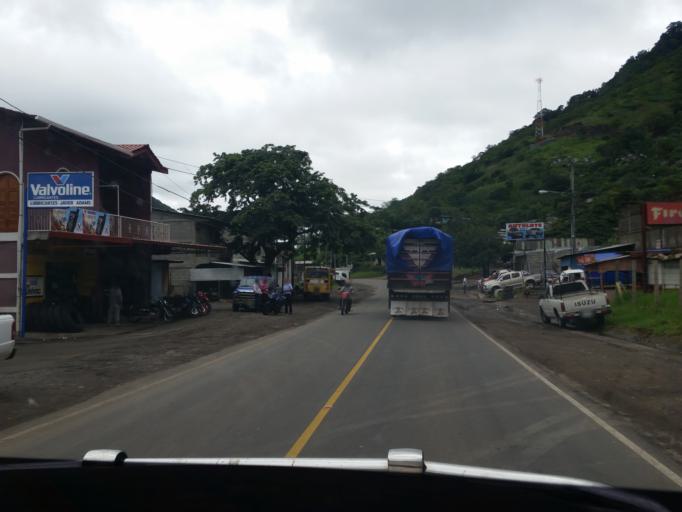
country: NI
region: Jinotega
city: Jinotega
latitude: 13.1030
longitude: -86.0012
